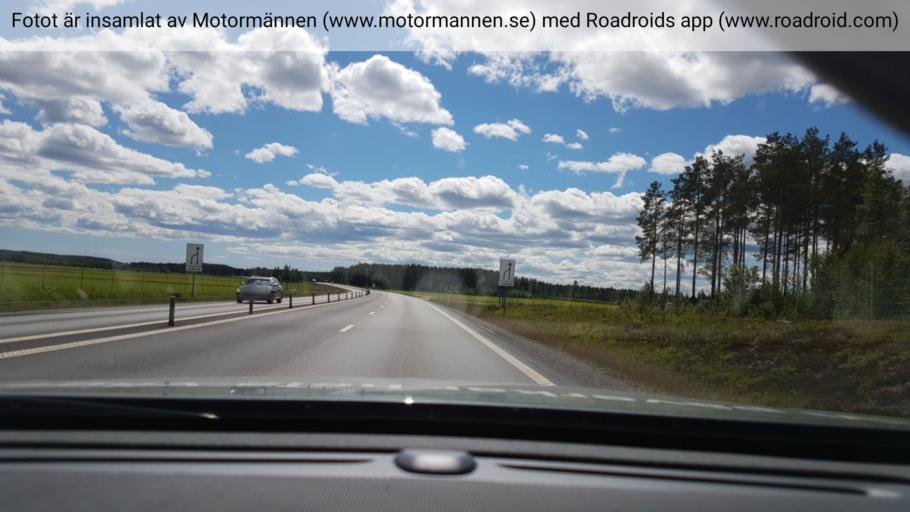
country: SE
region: Vaesterbotten
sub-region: Robertsfors Kommun
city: Robertsfors
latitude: 64.1061
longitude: 20.8740
